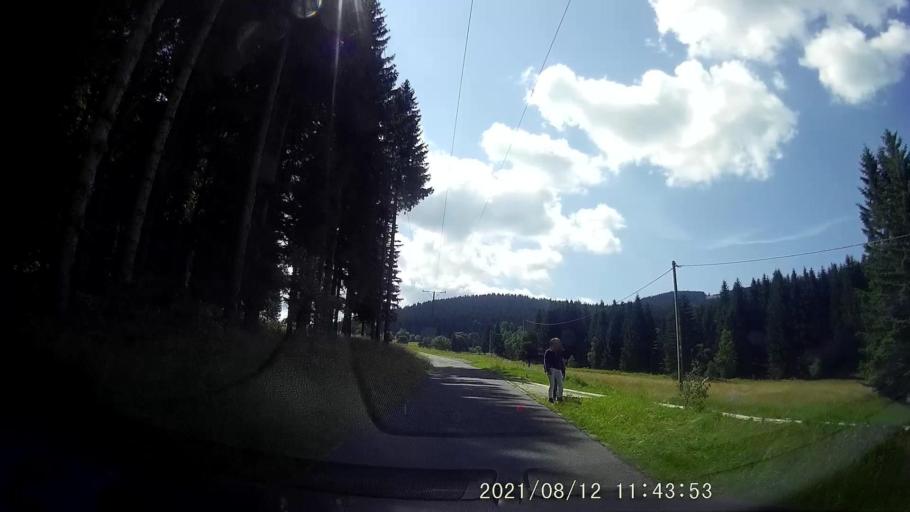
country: PL
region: Lower Silesian Voivodeship
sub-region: Powiat klodzki
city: Stronie Slaskie
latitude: 50.2596
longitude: 16.8342
